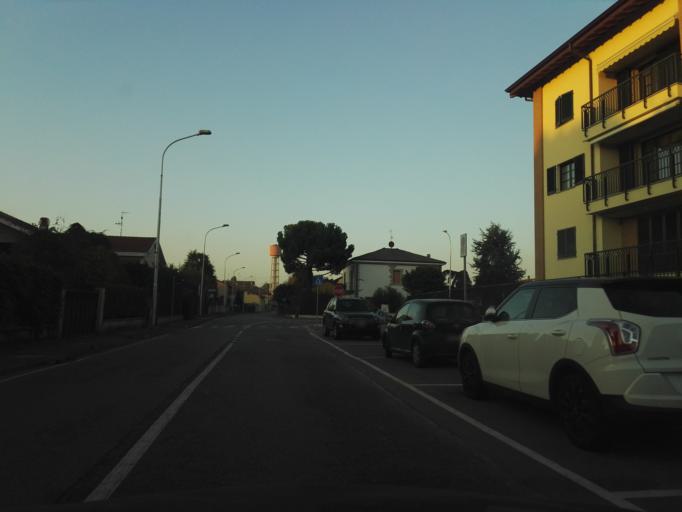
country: IT
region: Lombardy
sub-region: Citta metropolitana di Milano
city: Pantigliate
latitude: 45.4375
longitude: 9.3557
